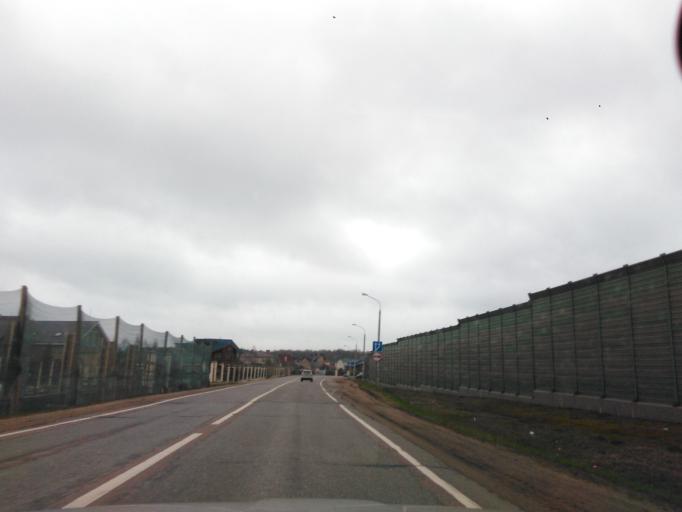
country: RU
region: Moskovskaya
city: Snegiri
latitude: 55.8430
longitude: 36.9822
